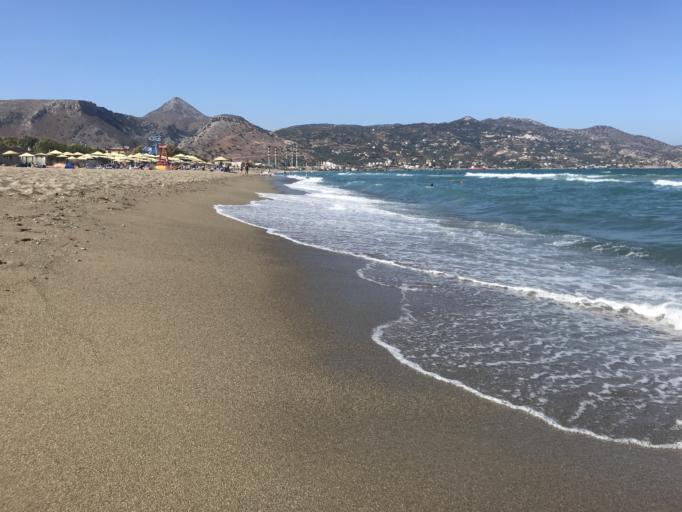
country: GR
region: Crete
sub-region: Nomos Irakleiou
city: Gazi
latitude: 35.3381
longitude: 25.0746
